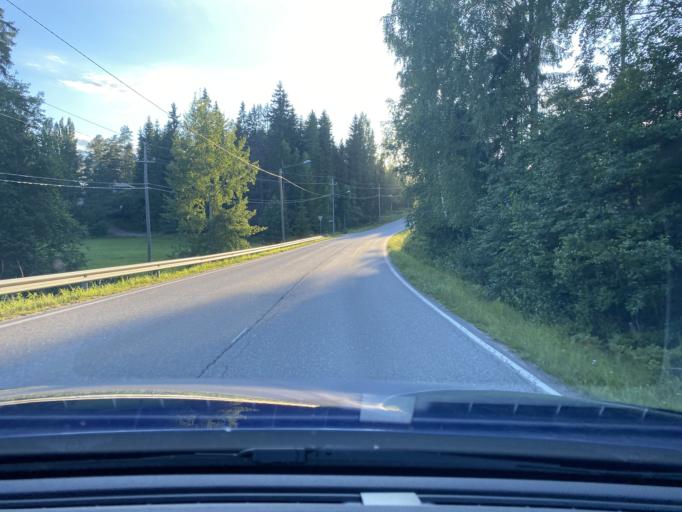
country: FI
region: Uusimaa
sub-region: Helsinki
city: Nurmijaervi
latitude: 60.4057
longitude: 24.7872
